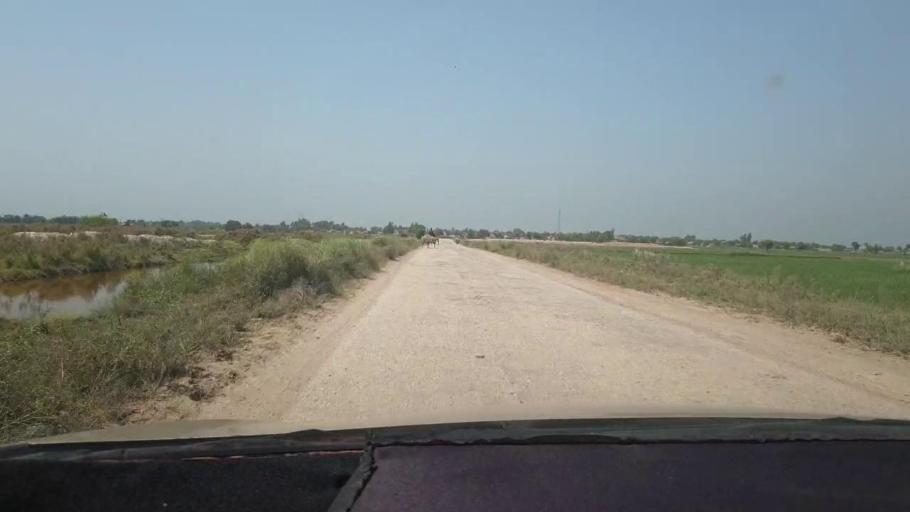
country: PK
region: Sindh
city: Miro Khan
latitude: 27.6652
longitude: 68.0700
